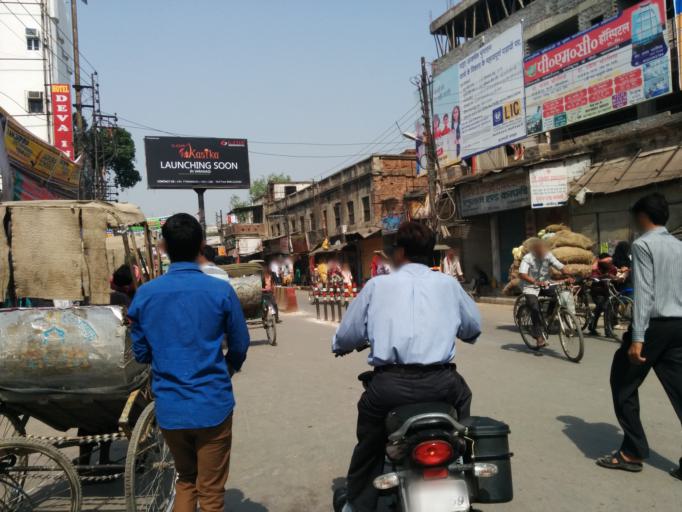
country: IN
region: Uttar Pradesh
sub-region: Varanasi
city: Varanasi
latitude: 25.3092
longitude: 83.0067
